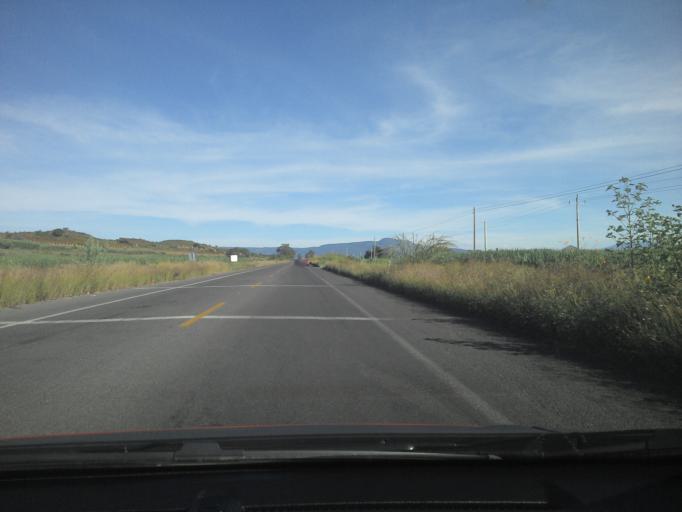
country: MX
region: Jalisco
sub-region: Teuchitlan
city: La Estanzuela
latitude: 20.6685
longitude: -103.7974
